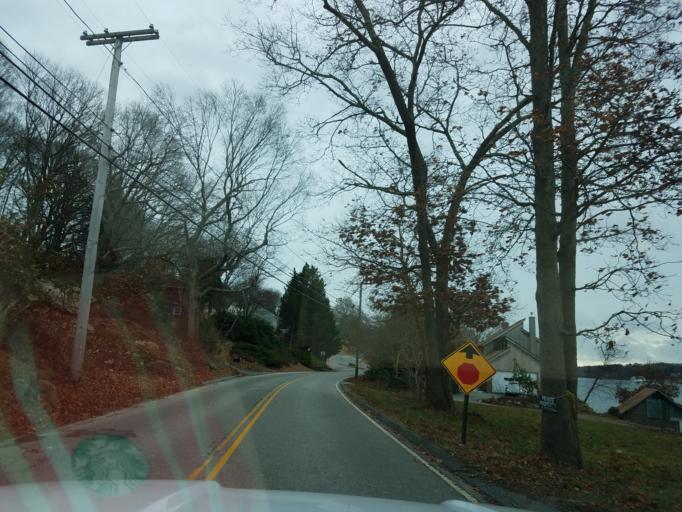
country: US
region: Connecticut
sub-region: New London County
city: Conning Towers-Nautilus Park
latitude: 41.3840
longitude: -72.0866
